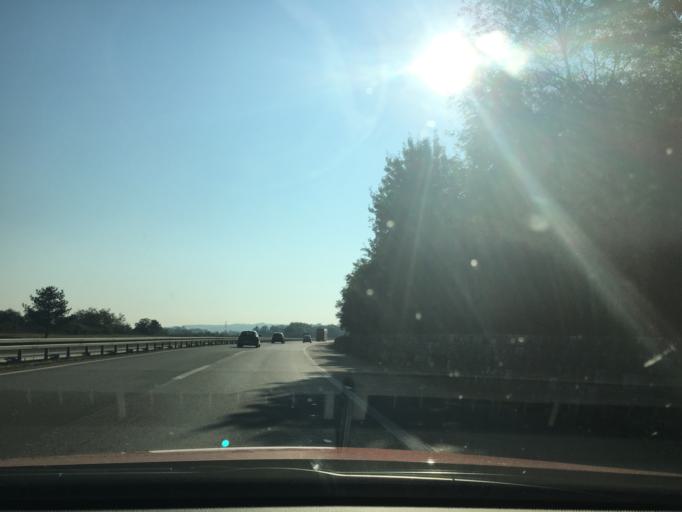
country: RS
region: Central Serbia
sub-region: Podunavski Okrug
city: Smederevo
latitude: 44.5791
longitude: 20.8828
